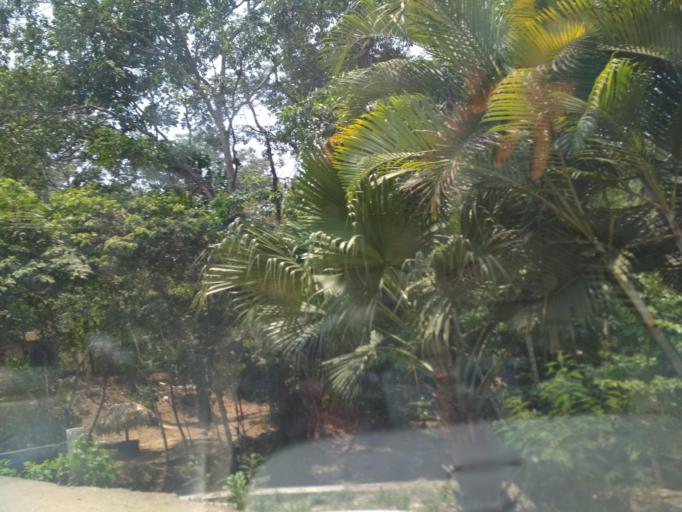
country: MX
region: Veracruz
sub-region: Tezonapa
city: Laguna Chica (Pueblo Nuevo)
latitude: 18.5707
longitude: -96.7312
